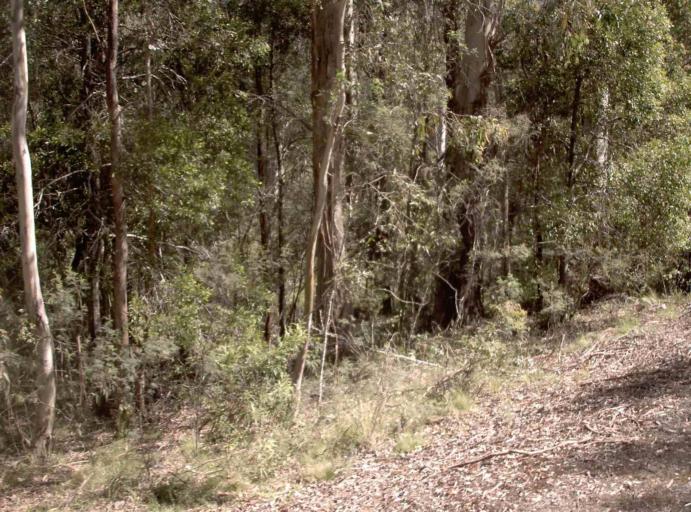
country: AU
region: New South Wales
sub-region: Bombala
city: Bombala
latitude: -37.1598
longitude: 148.7217
